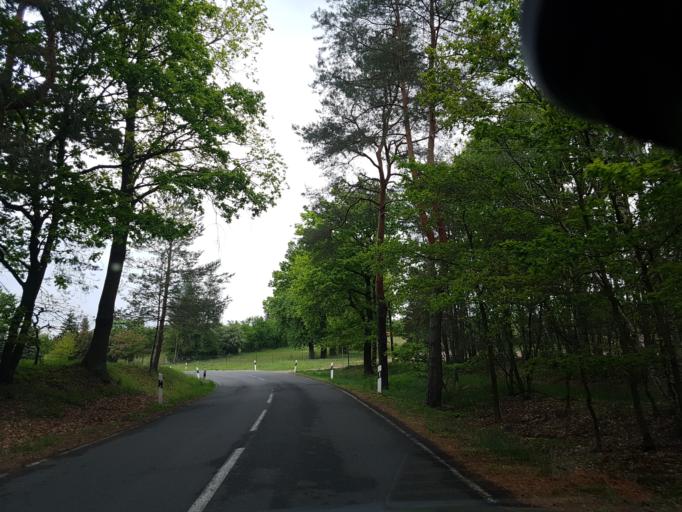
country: DE
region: Brandenburg
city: Crinitz
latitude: 51.7600
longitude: 13.7511
